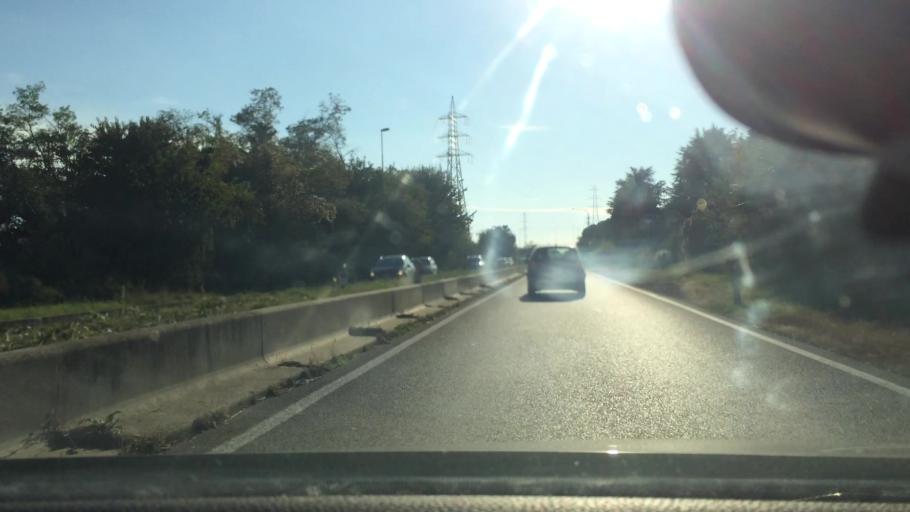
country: IT
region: Lombardy
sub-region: Citta metropolitana di Milano
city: Villa Cortese
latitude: 45.5607
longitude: 8.8933
